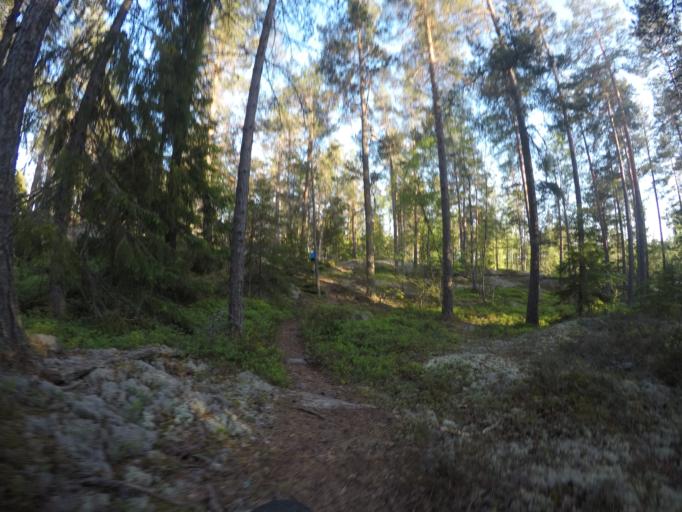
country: SE
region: Soedermanland
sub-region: Eskilstuna Kommun
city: Eskilstuna
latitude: 59.3352
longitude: 16.5236
